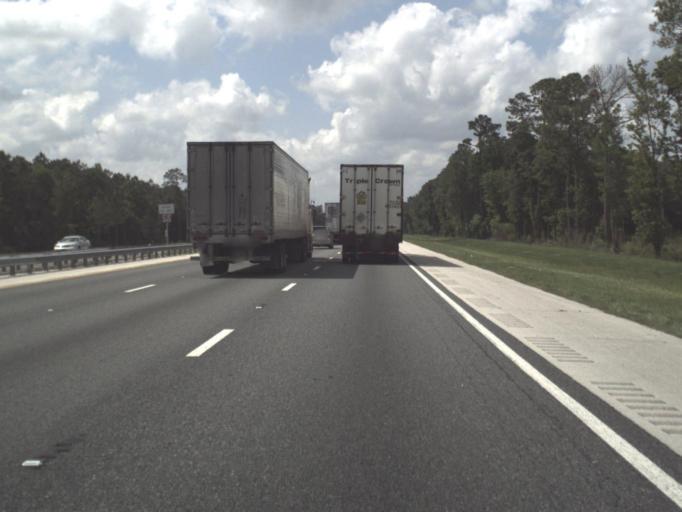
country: US
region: Florida
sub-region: Saint Johns County
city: Villano Beach
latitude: 29.9566
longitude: -81.4438
